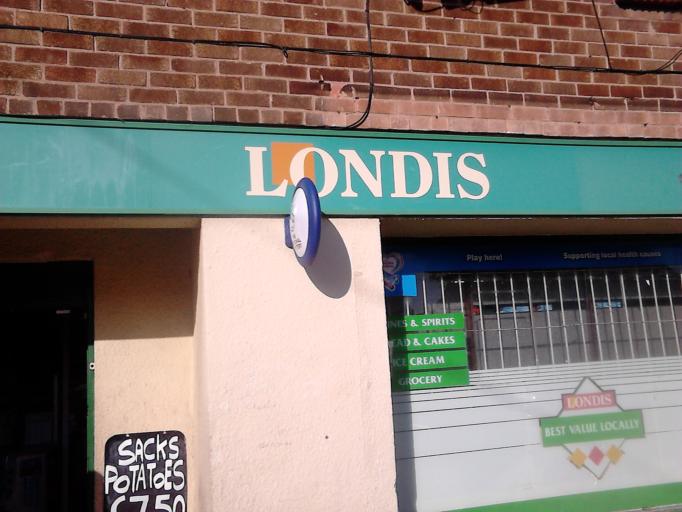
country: GB
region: England
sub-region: Nottinghamshire
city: Newark on Trent
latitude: 53.0632
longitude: -0.8135
